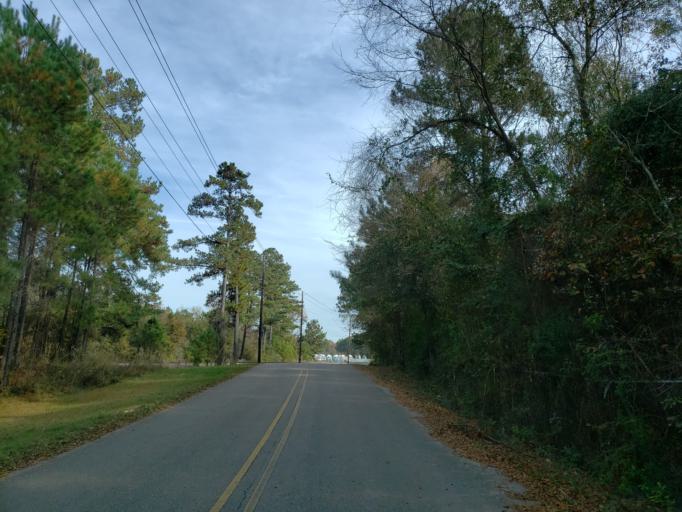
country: US
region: Mississippi
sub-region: Forrest County
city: Glendale
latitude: 31.3494
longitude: -89.3201
